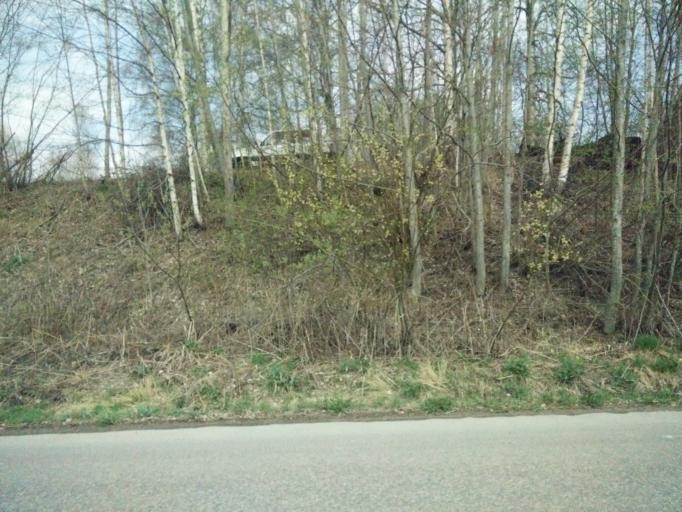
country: SE
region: Vaermland
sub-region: Munkfors Kommun
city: Munkfors
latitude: 59.8394
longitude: 13.5450
